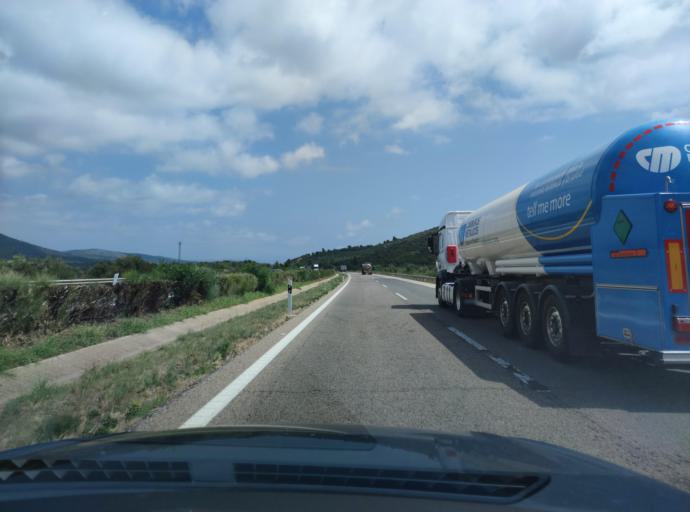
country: ES
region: Valencia
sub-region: Provincia de Castello
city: Santa Magdalena de Pulpis
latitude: 40.3768
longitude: 0.3379
